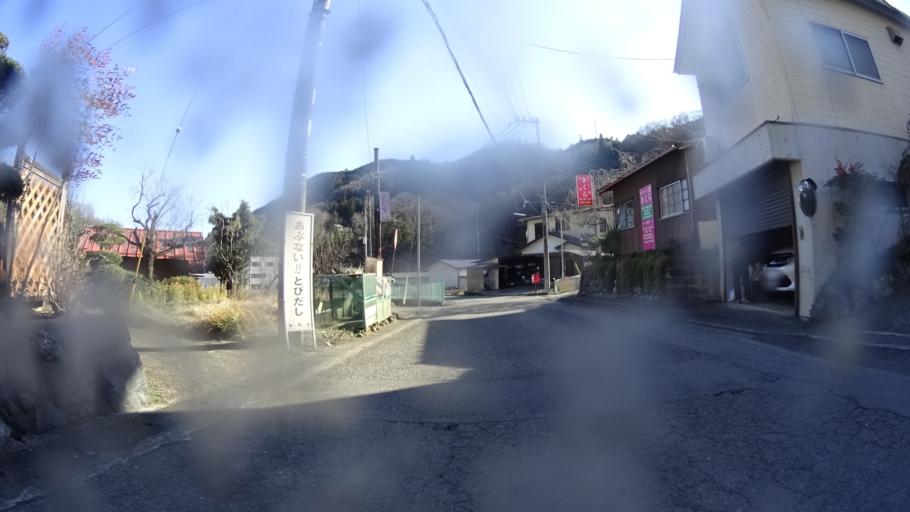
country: JP
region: Yamanashi
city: Uenohara
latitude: 35.6220
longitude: 139.1532
